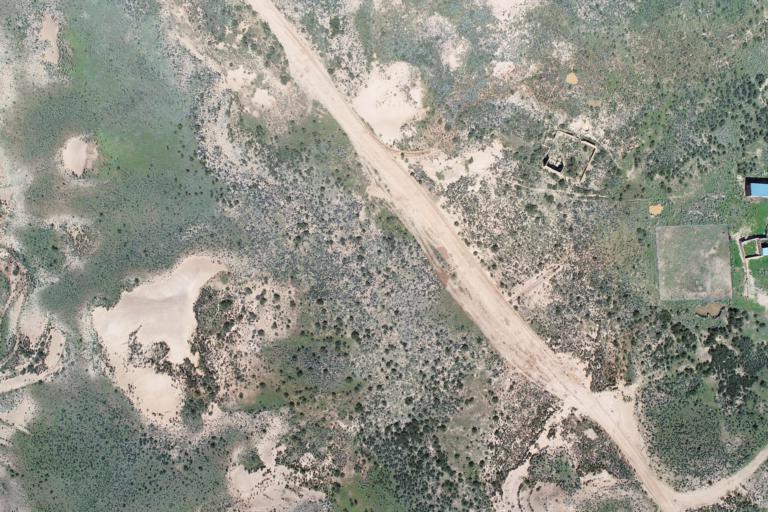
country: BO
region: La Paz
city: Curahuara de Carangas
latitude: -17.2924
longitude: -68.5123
